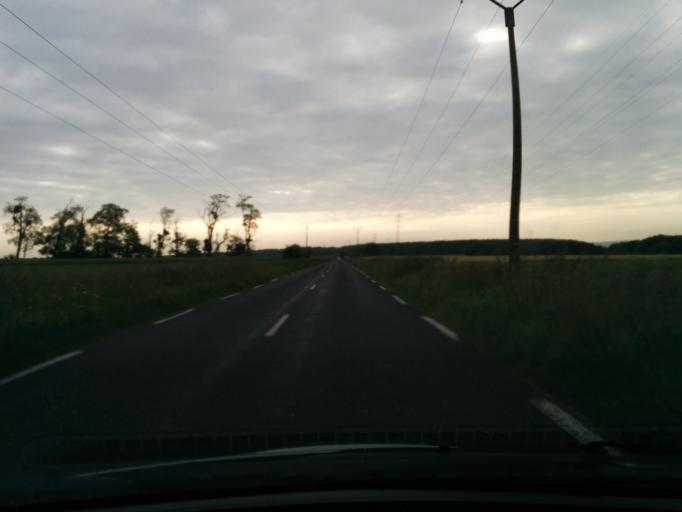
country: FR
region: Ile-de-France
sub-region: Departement des Yvelines
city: Limetz-Villez
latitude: 49.0942
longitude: 1.5548
